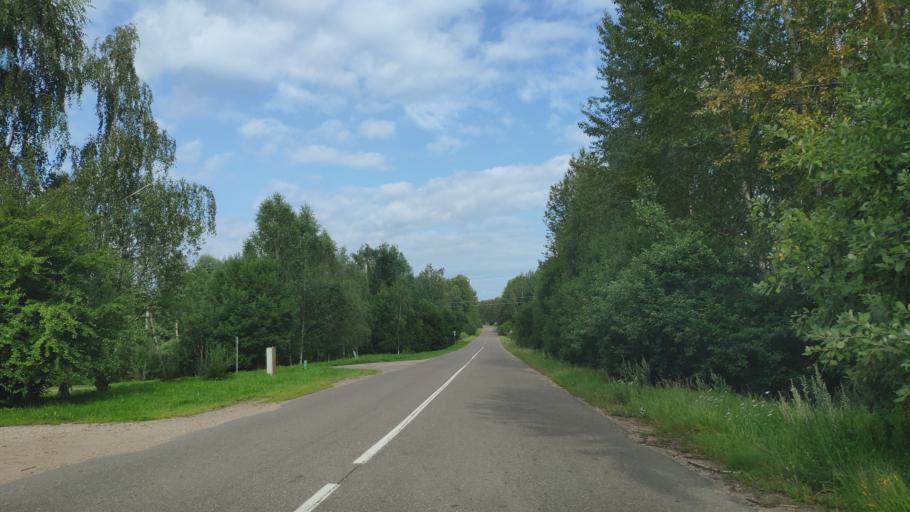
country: BY
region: Minsk
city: Khatsyezhyna
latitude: 53.8753
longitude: 27.2949
